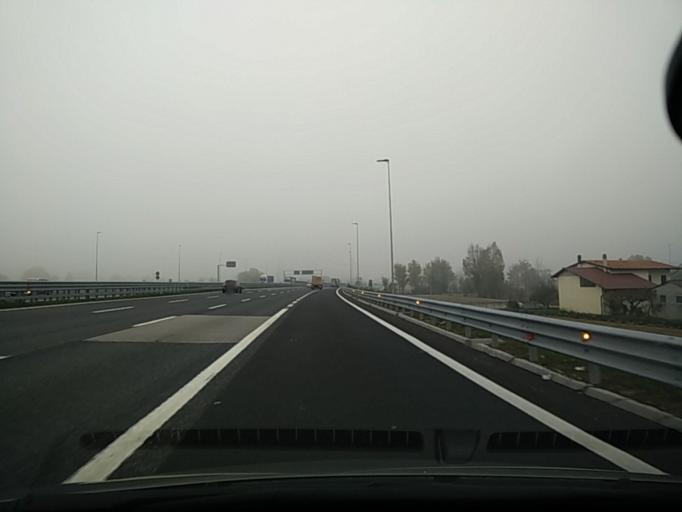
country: IT
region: Veneto
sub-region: Provincia di Venezia
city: Martellago
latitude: 45.5606
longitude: 12.1502
